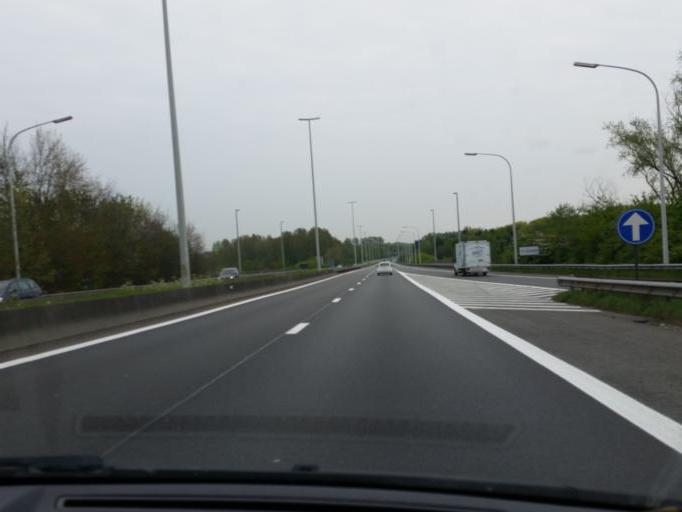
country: BE
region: Flanders
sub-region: Provincie Oost-Vlaanderen
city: Melle
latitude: 51.0121
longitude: 3.7924
